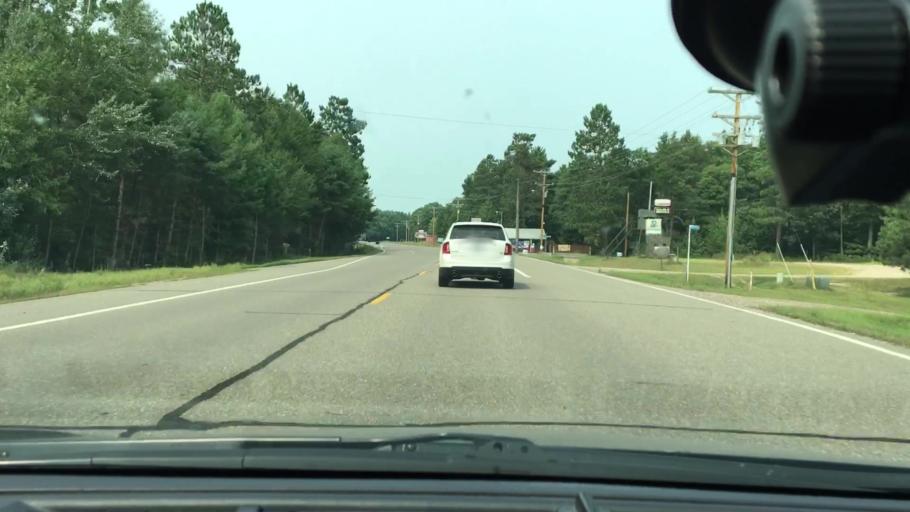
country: US
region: Minnesota
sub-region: Crow Wing County
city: Cross Lake
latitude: 46.5725
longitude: -94.1295
